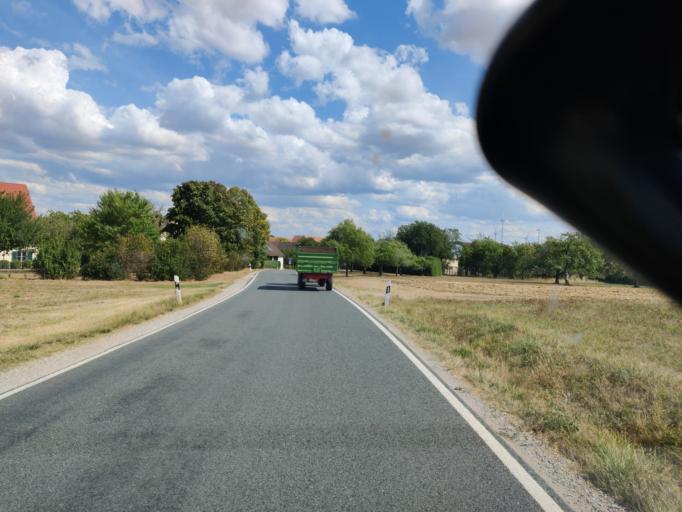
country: DE
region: Bavaria
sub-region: Regierungsbezirk Mittelfranken
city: Thalmassing
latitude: 49.0708
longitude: 11.2207
